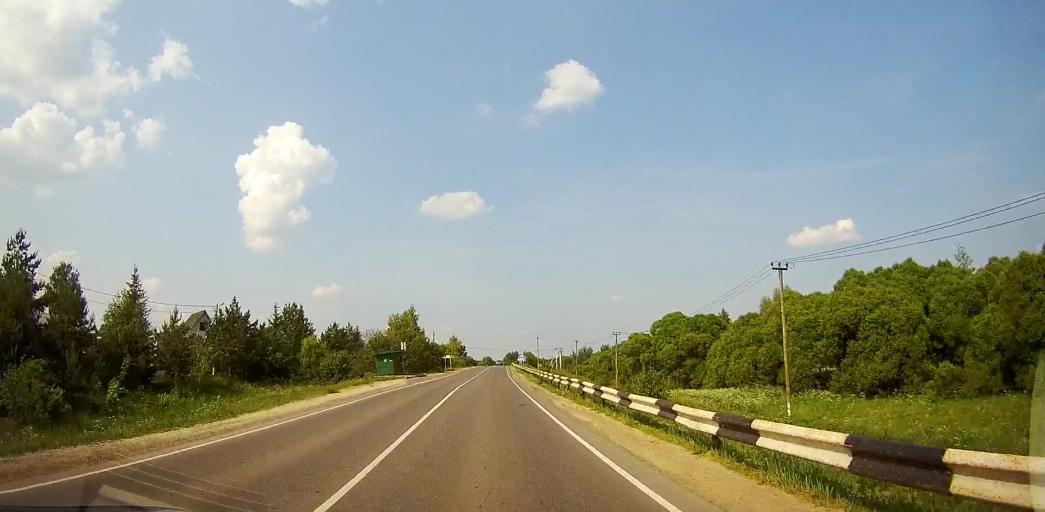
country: RU
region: Moskovskaya
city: Mikhnevo
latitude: 55.1827
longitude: 37.9745
